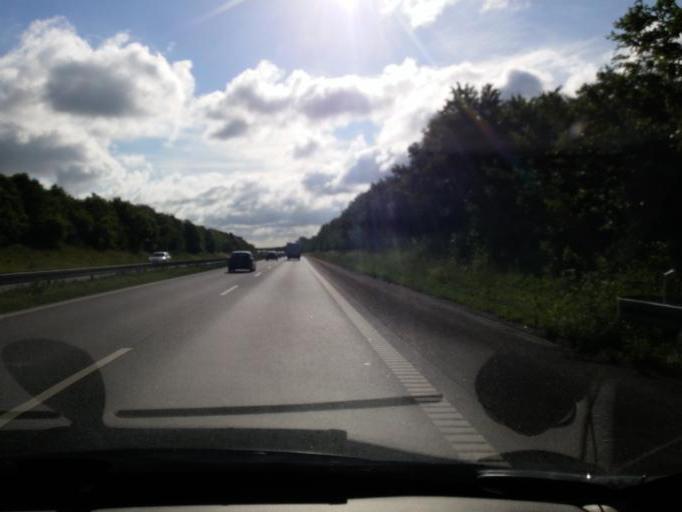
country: DK
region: Zealand
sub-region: Ringsted Kommune
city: Ringsted
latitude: 55.4538
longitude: 11.7241
